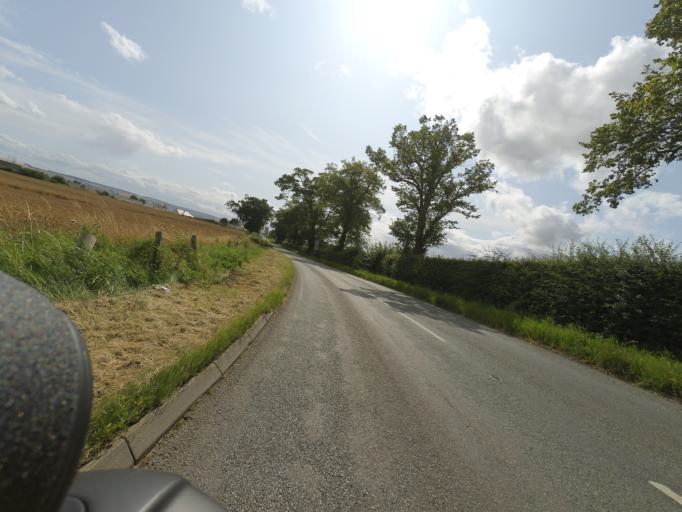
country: GB
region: Scotland
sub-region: Highland
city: Invergordon
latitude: 57.7282
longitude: -4.0955
